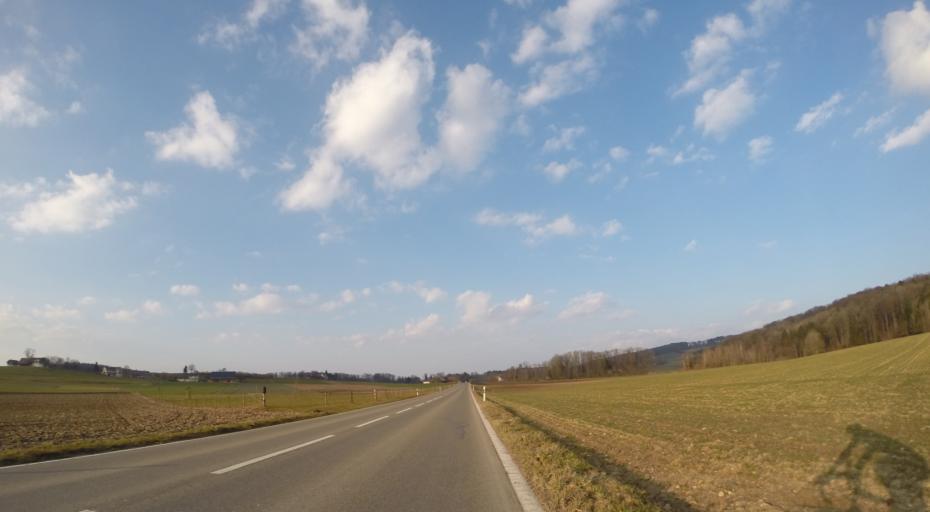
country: CH
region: Thurgau
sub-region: Frauenfeld District
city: Steckborn
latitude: 47.6393
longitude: 8.9755
